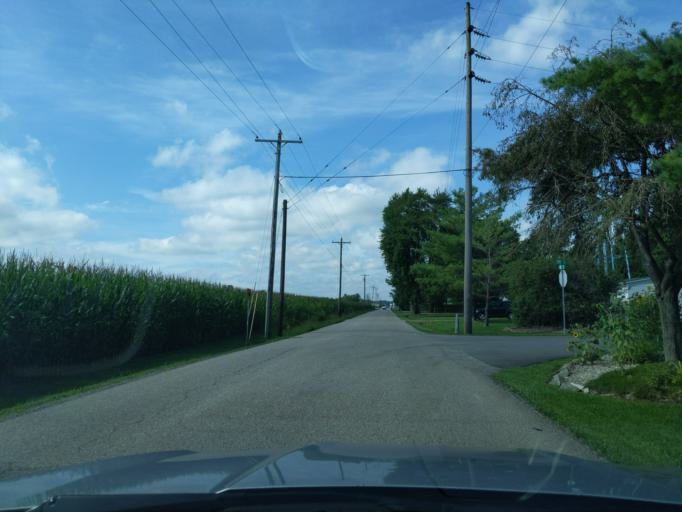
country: US
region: Indiana
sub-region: Ripley County
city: Batesville
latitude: 39.3091
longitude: -85.3477
